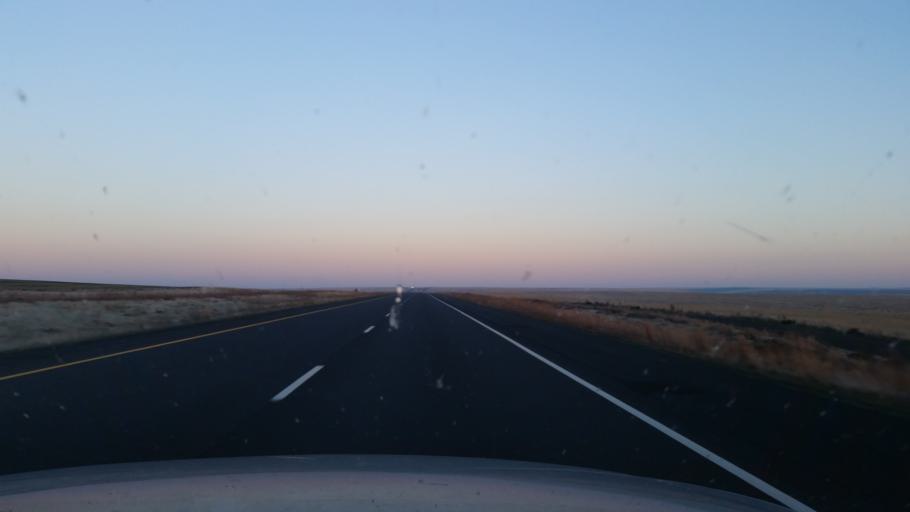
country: US
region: Washington
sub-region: Grant County
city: Warden
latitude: 47.0860
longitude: -118.7802
